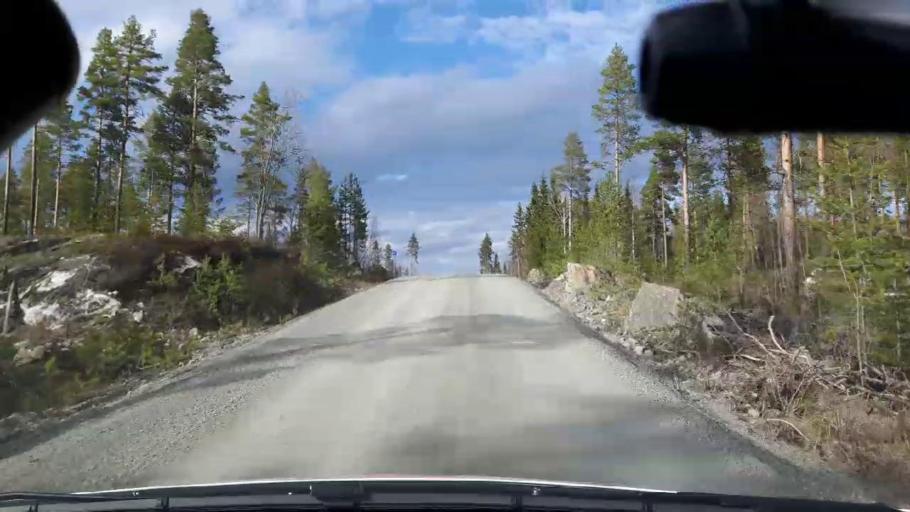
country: SE
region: Jaemtland
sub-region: Bergs Kommun
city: Hoverberg
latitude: 62.9245
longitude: 14.6424
